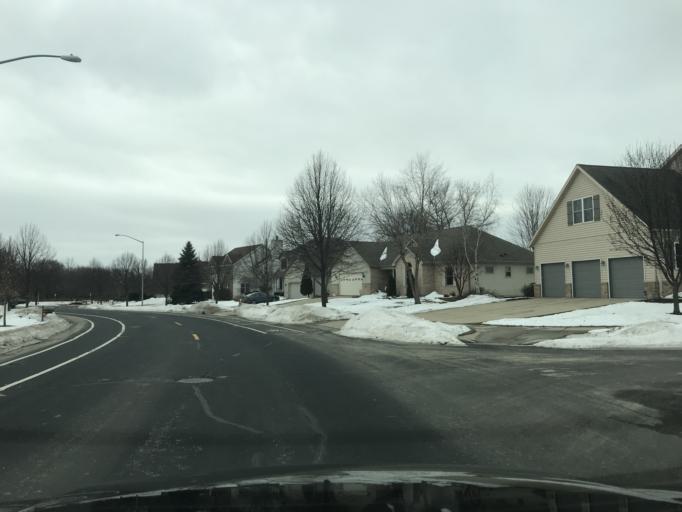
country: US
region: Wisconsin
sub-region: Dane County
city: Monona
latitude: 43.0816
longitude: -89.2729
